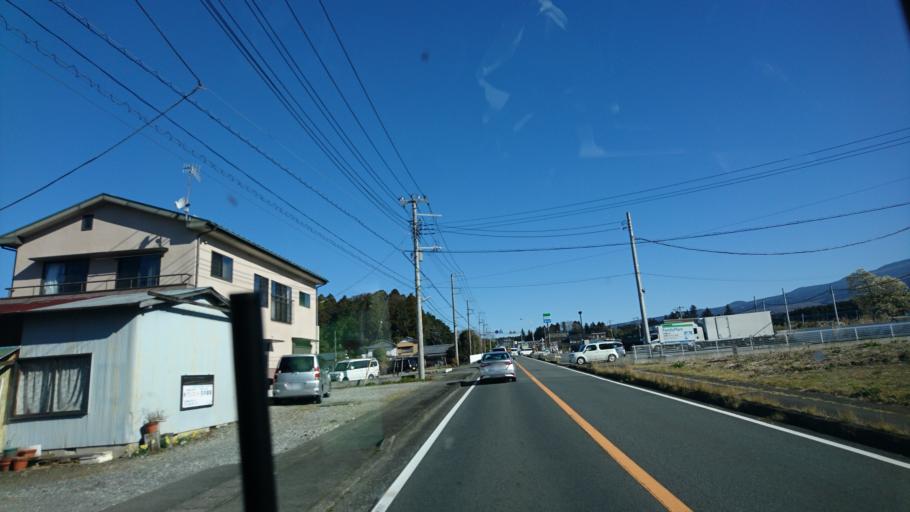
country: JP
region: Shizuoka
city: Fujinomiya
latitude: 35.2980
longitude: 138.5933
